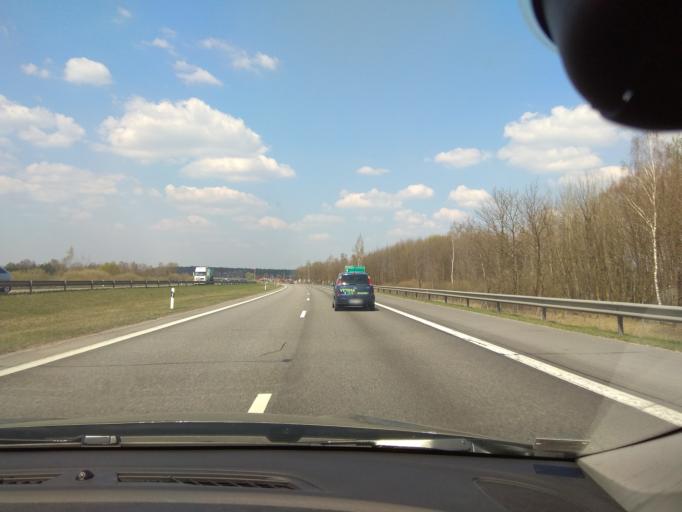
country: LT
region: Kauno apskritis
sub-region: Kaunas
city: Sargenai
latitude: 55.0908
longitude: 23.8092
